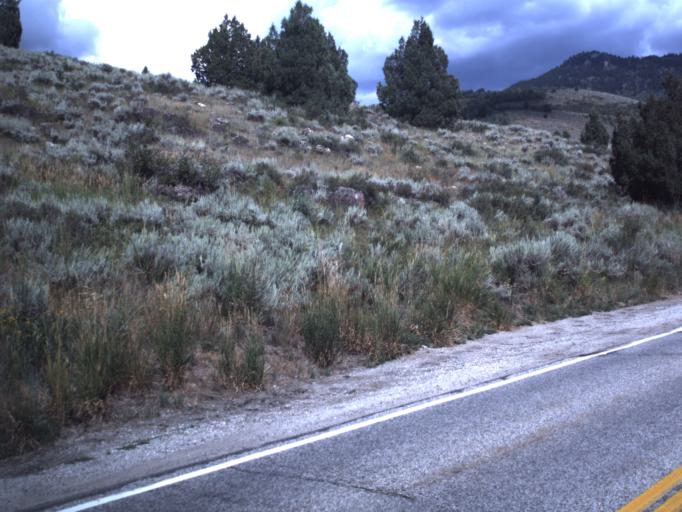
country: US
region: Utah
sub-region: Cache County
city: North Logan
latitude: 41.8563
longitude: -111.5838
